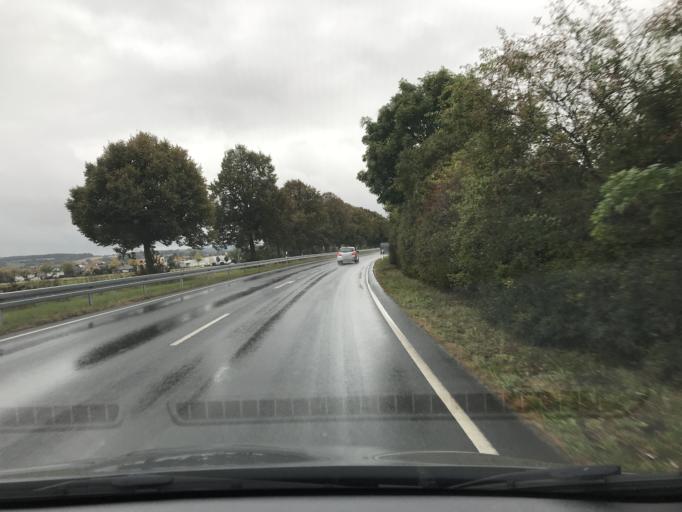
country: DE
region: Bavaria
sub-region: Regierungsbezirk Unterfranken
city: Grossostheim
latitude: 49.9304
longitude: 9.0861
